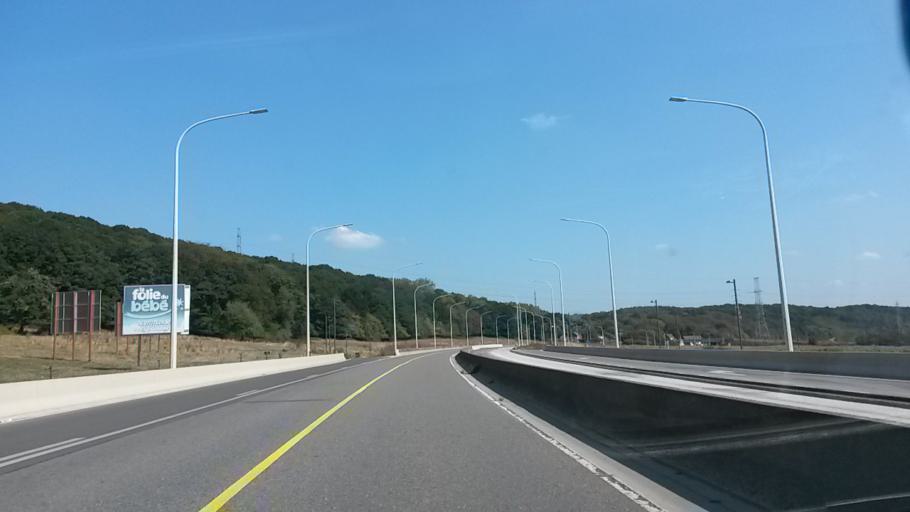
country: BE
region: Wallonia
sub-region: Province du Hainaut
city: Farciennes
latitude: 50.4422
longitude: 4.5487
